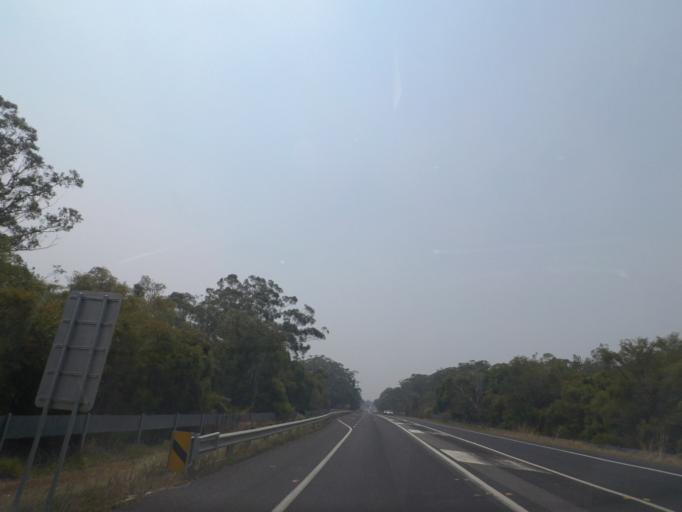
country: AU
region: New South Wales
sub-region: Ballina
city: Ballina
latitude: -28.9279
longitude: 153.4755
